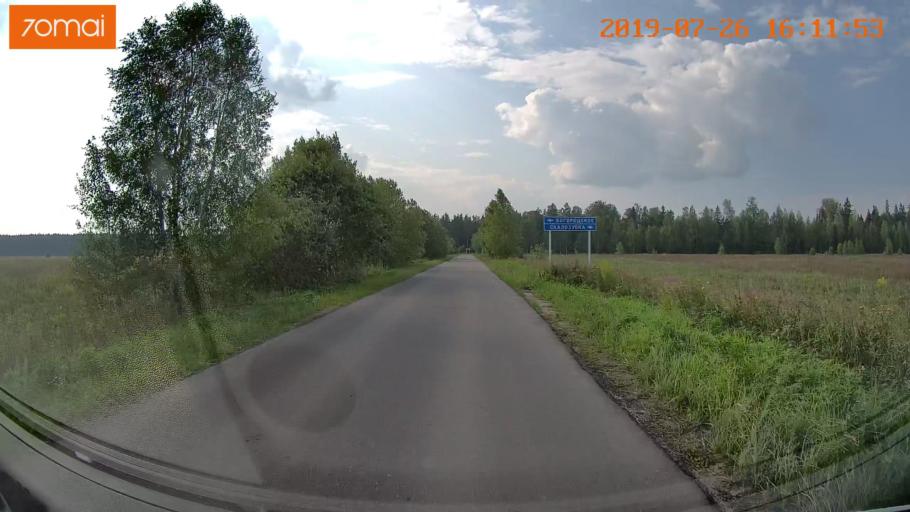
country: RU
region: Ivanovo
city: Bogorodskoye
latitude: 57.0674
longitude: 41.0537
